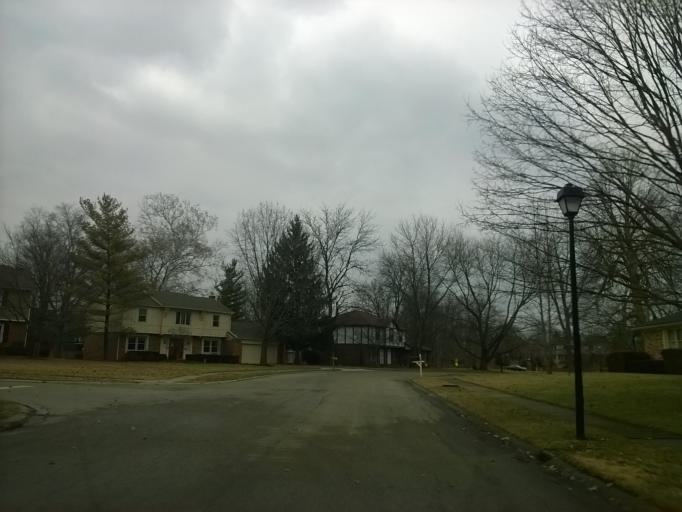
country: US
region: Indiana
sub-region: Hamilton County
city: Carmel
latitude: 39.9425
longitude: -86.1022
